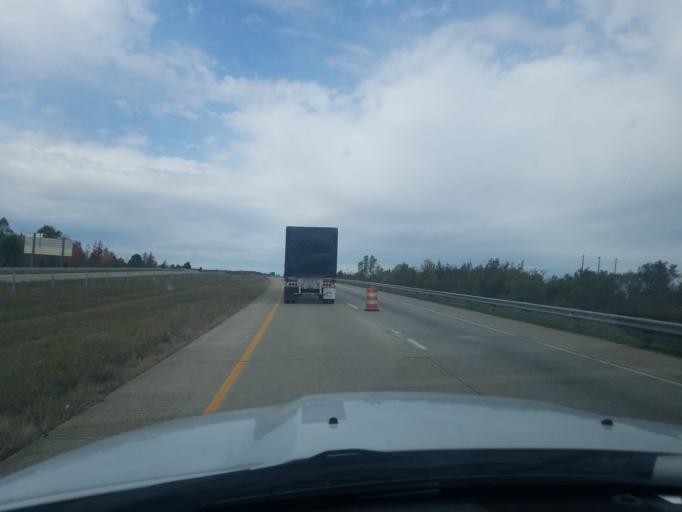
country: US
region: Indiana
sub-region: Vanderburgh County
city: Melody Hill
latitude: 38.1094
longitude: -87.4763
